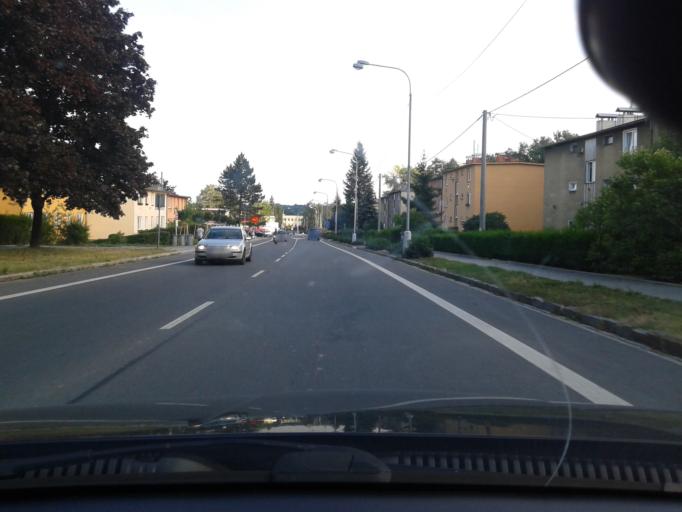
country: CZ
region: Moravskoslezsky
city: Orlova
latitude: 49.8623
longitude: 18.4232
